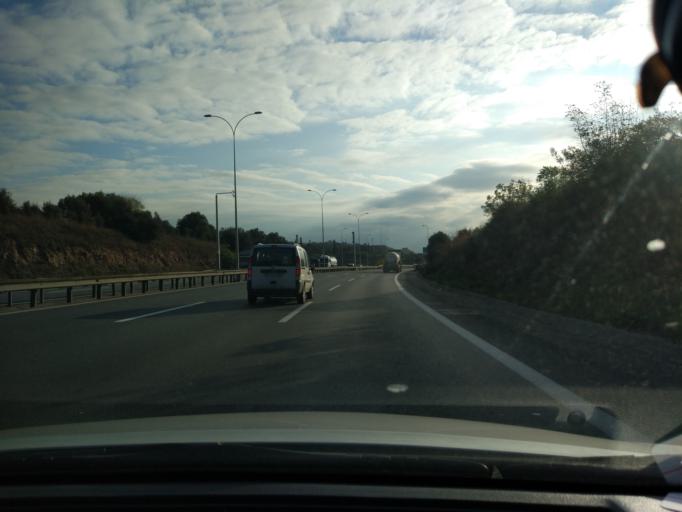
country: TR
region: Kocaeli
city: Tavsancil
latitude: 40.7732
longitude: 29.5569
